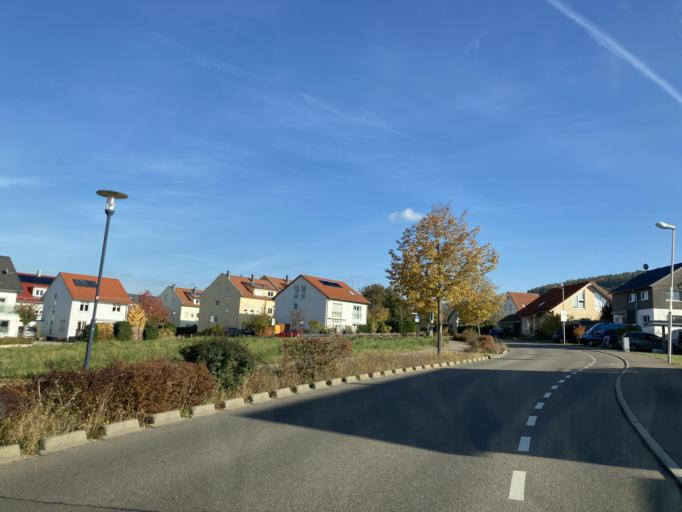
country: DE
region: Baden-Wuerttemberg
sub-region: Tuebingen Region
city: Mossingen
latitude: 48.4018
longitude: 9.0602
